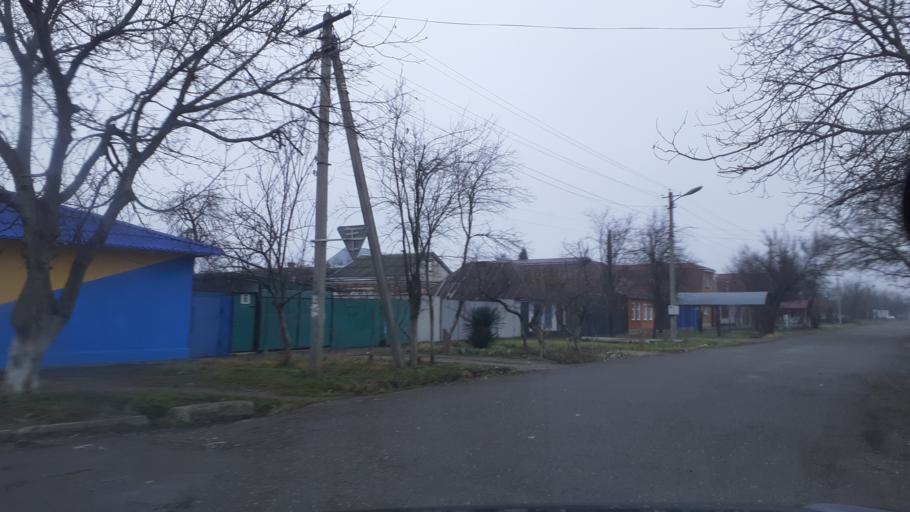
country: RU
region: Adygeya
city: Maykop
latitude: 44.6192
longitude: 40.0905
